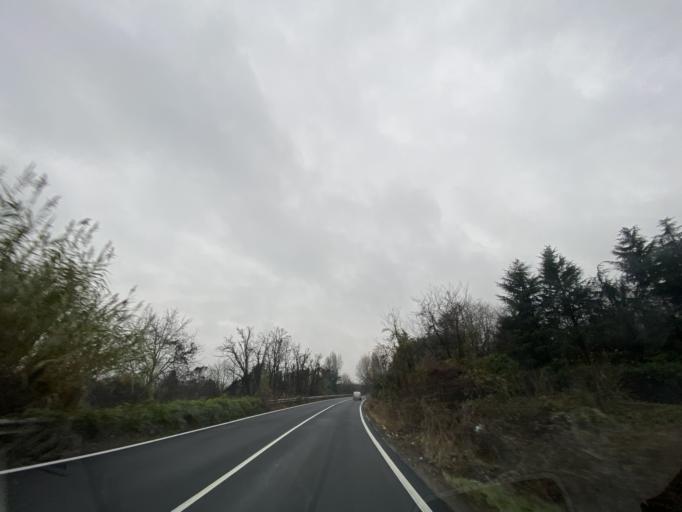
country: IT
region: Lombardy
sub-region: Citta metropolitana di Milano
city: Cusago
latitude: 45.4493
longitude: 9.0465
